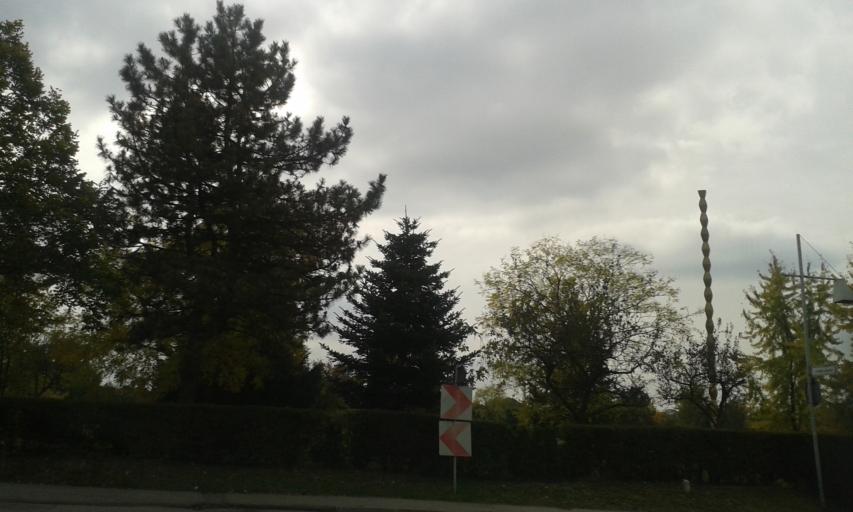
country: RO
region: Gorj
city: Targu Jiu
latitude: 45.0380
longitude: 23.2863
